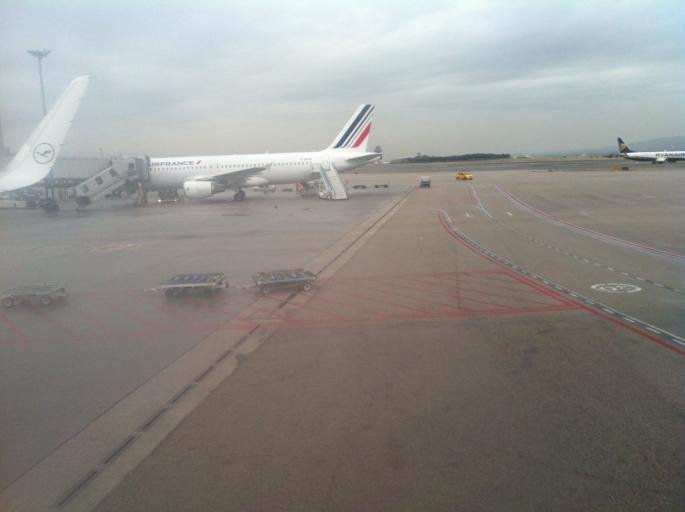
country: ES
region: Madrid
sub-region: Provincia de Madrid
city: Barajas de Madrid
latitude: 40.4720
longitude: -3.5698
